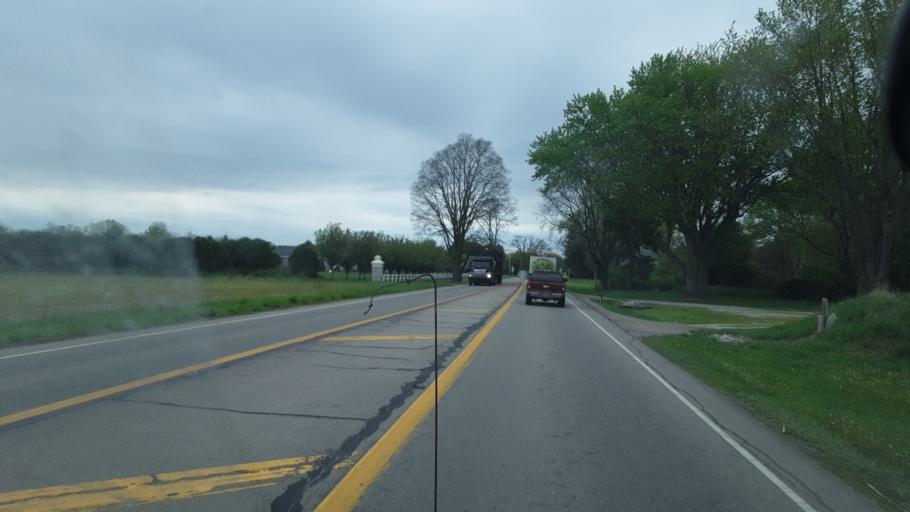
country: US
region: Indiana
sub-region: Elkhart County
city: New Paris
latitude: 41.5184
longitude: -85.7714
